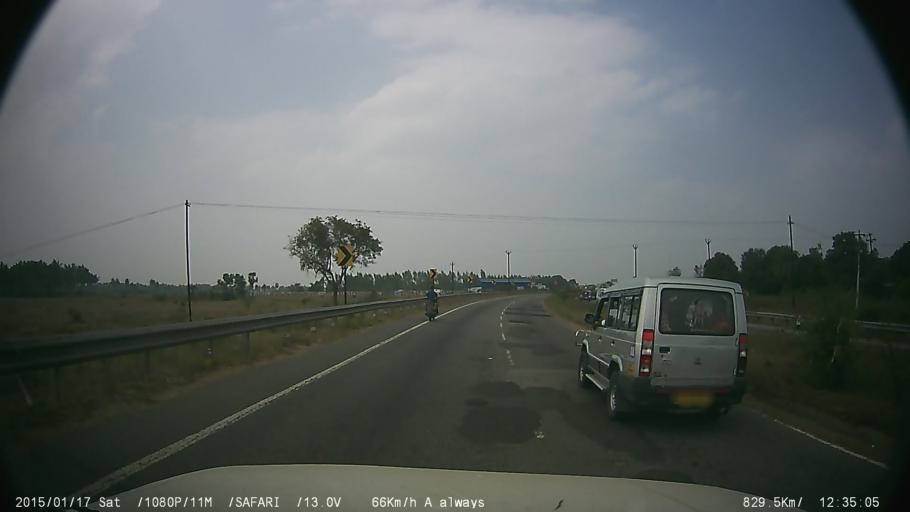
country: IN
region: Tamil Nadu
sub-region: Kancheepuram
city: Kanchipuram
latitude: 12.8744
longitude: 79.6164
